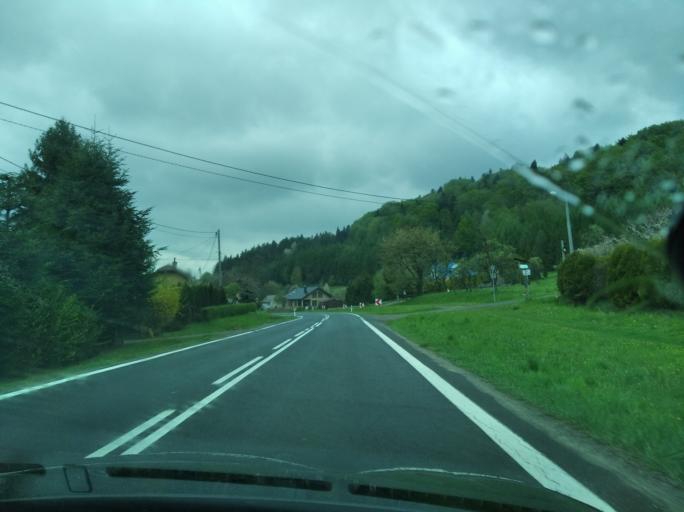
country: PL
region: Subcarpathian Voivodeship
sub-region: Powiat sanocki
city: Zagorz
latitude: 49.5456
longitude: 22.2714
